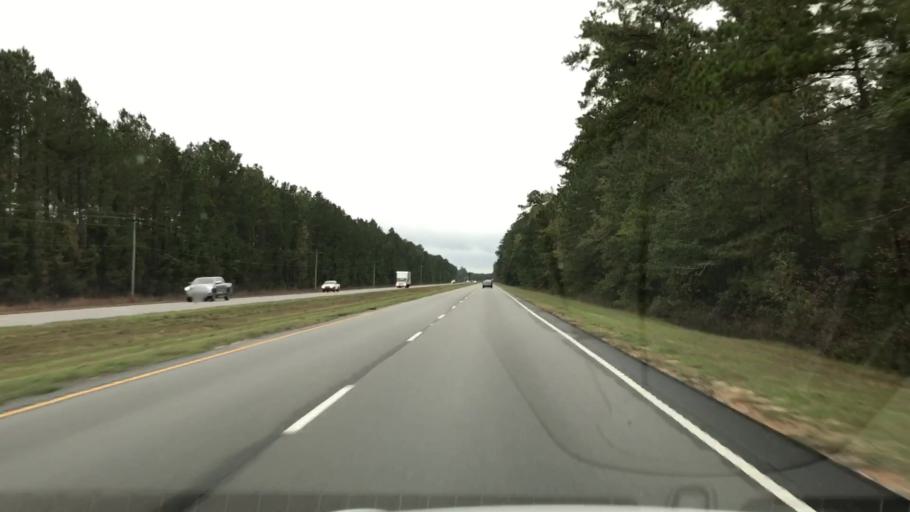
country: US
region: South Carolina
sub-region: Georgetown County
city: Georgetown
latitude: 33.2797
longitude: -79.3508
